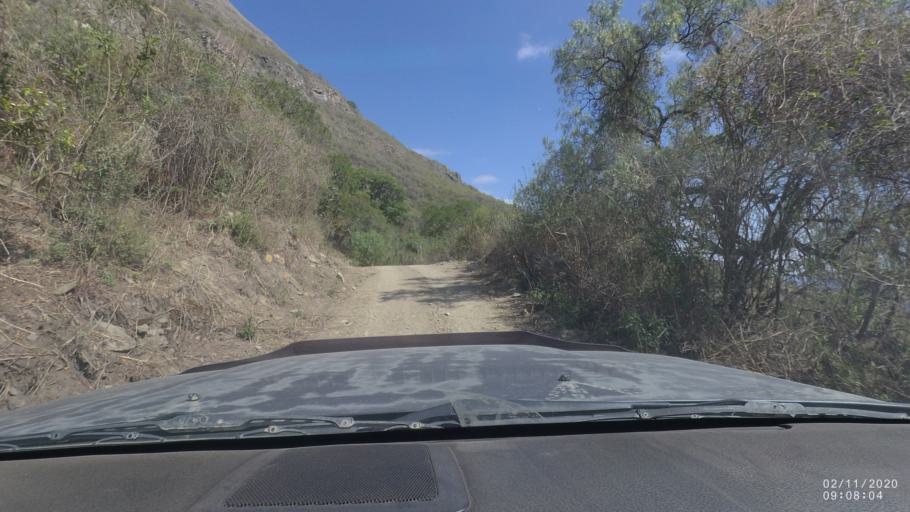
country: BO
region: Chuquisaca
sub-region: Provincia Zudanez
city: Mojocoya
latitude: -18.5272
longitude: -64.5628
